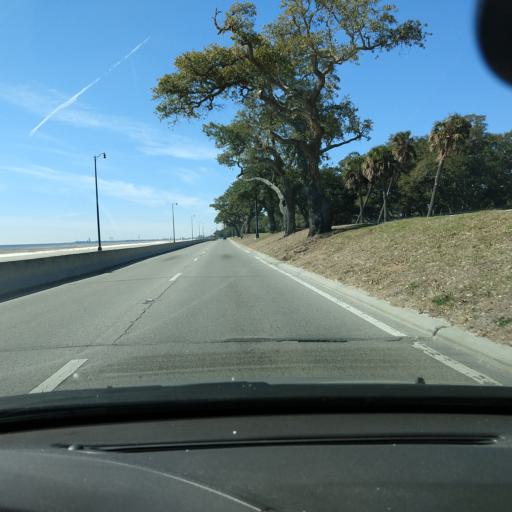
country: US
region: Mississippi
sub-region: Harrison County
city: Gulfport
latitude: 30.3846
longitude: -89.0171
